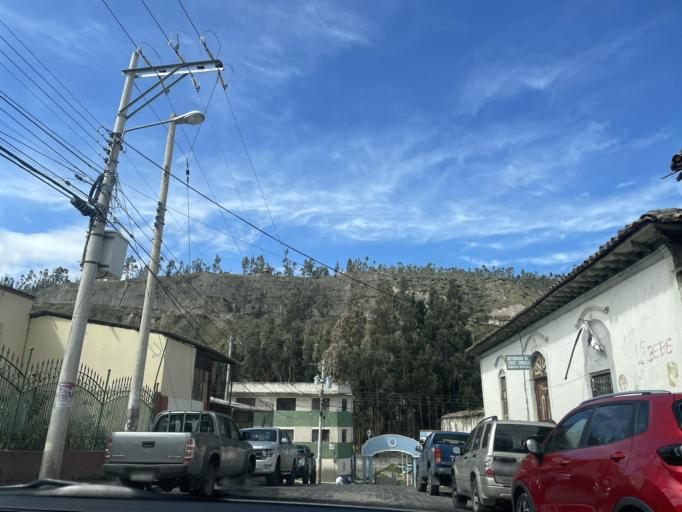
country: EC
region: Chimborazo
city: Guano
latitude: -1.6083
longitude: -78.6445
